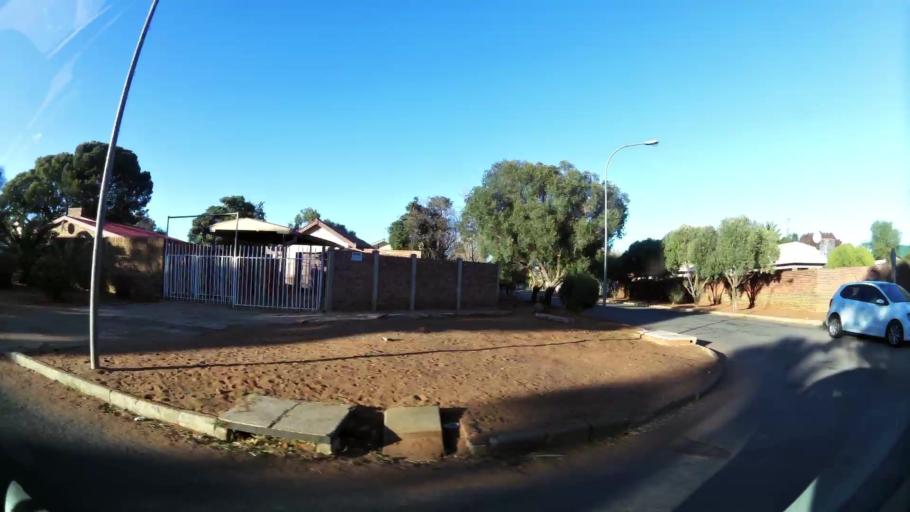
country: ZA
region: Northern Cape
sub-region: Frances Baard District Municipality
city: Kimberley
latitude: -28.7532
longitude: 24.7436
